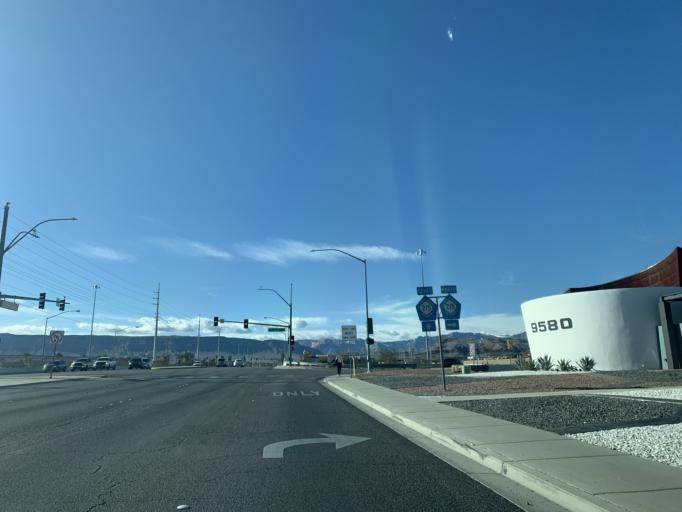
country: US
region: Nevada
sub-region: Clark County
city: Summerlin South
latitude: 36.1152
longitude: -115.3008
